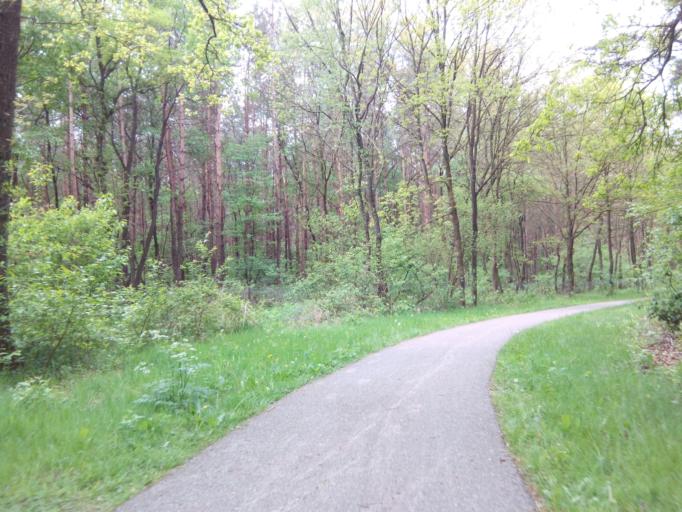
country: NL
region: Gelderland
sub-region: Gemeente Ede
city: Otterlo
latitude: 52.0875
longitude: 5.7647
